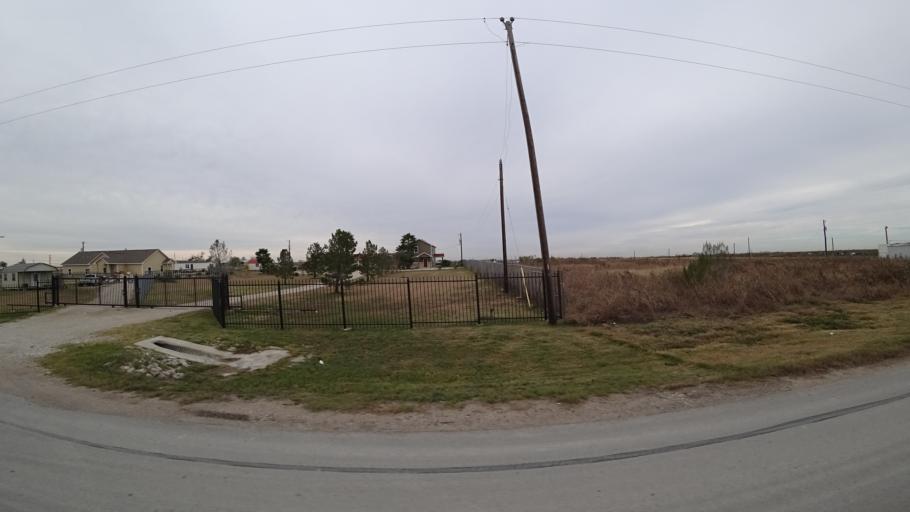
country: US
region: Texas
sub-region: Travis County
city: Garfield
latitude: 30.1046
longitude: -97.6164
